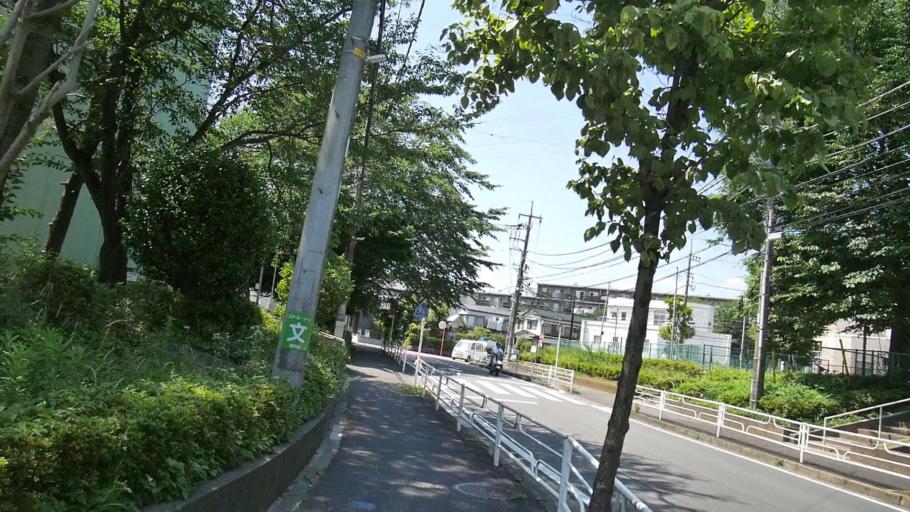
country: JP
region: Kanagawa
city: Fujisawa
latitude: 35.4003
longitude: 139.5190
